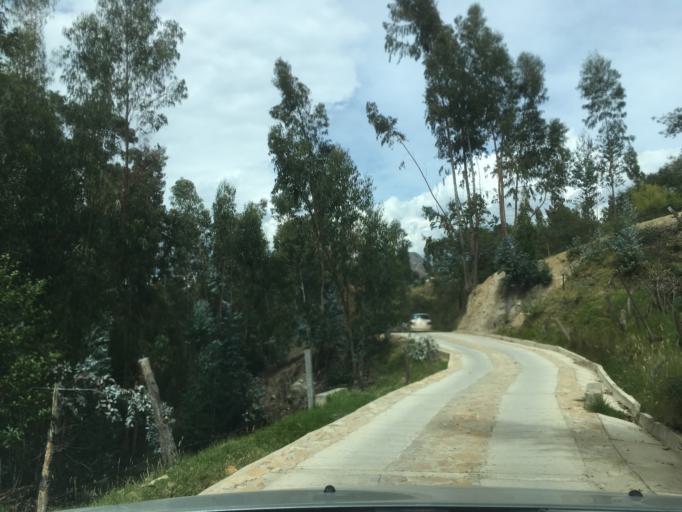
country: CO
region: Boyaca
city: Pesca
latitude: 5.5760
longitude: -72.9682
